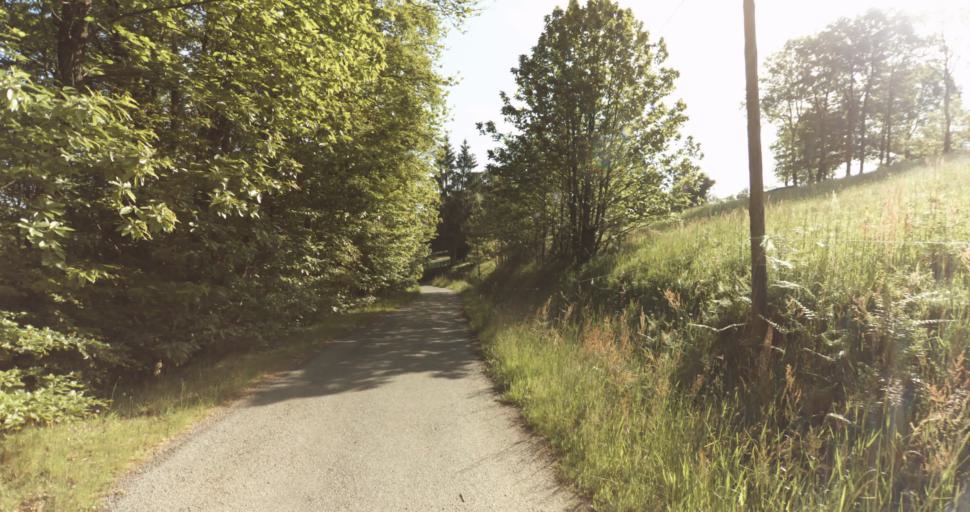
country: FR
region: Limousin
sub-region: Departement de la Haute-Vienne
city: Solignac
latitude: 45.7324
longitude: 1.2424
